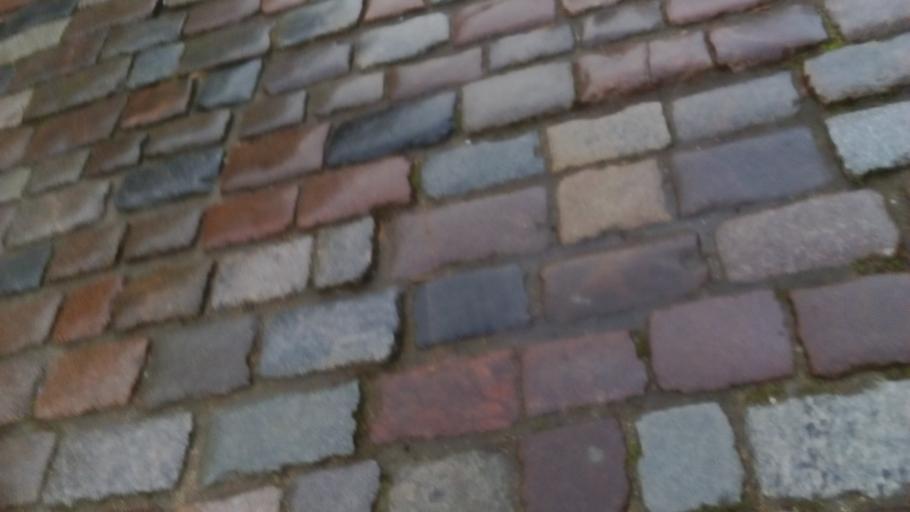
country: LT
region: Kauno apskritis
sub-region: Kaunas
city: Kaunas
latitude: 54.8967
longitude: 23.8958
